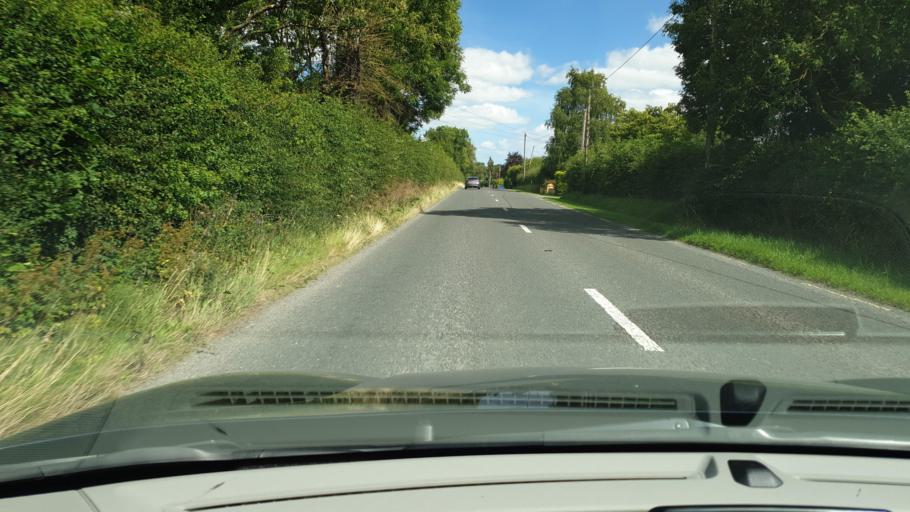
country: IE
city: Confey
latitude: 53.4375
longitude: -6.5364
